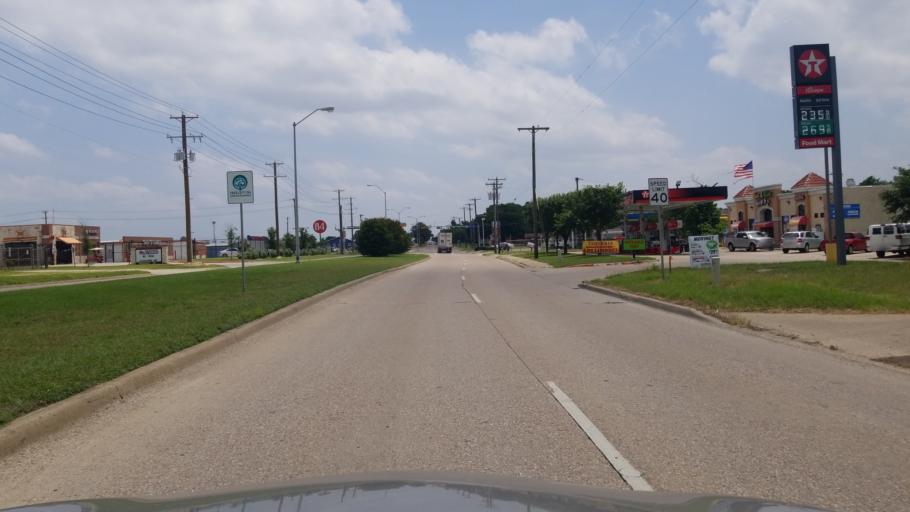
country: US
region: Texas
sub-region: Dallas County
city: Duncanville
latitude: 32.6762
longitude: -96.9086
